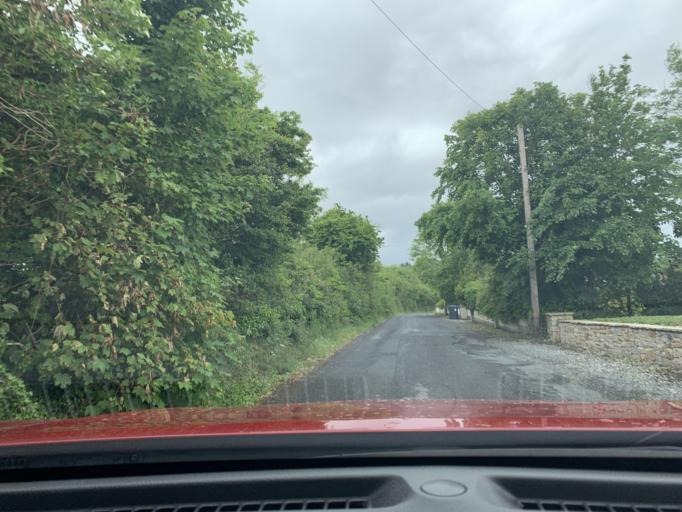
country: IE
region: Connaught
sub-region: Sligo
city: Sligo
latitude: 54.3122
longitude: -8.4767
